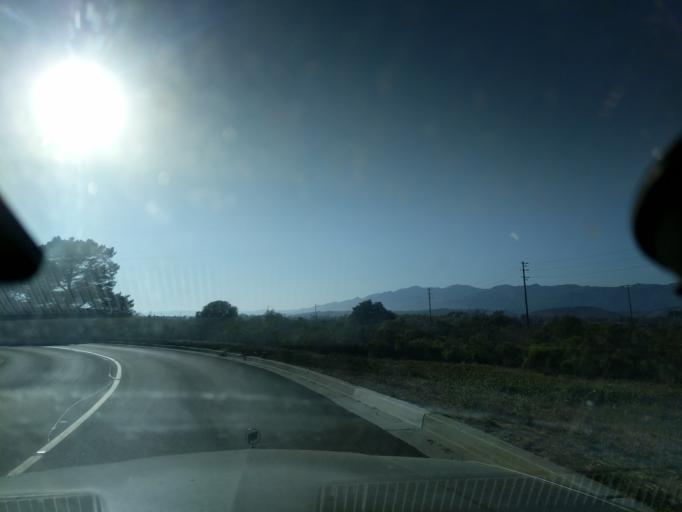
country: US
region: California
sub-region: Santa Barbara County
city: Isla Vista
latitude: 34.4229
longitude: -119.8545
